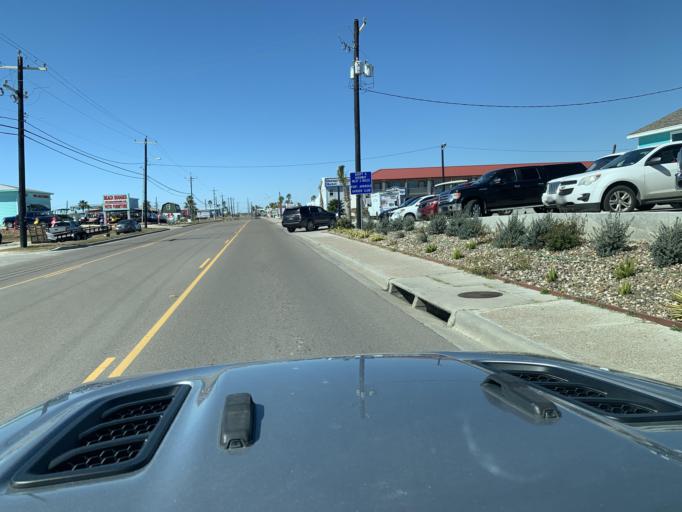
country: US
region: Texas
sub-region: Nueces County
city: Port Aransas
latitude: 27.8290
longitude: -97.0681
